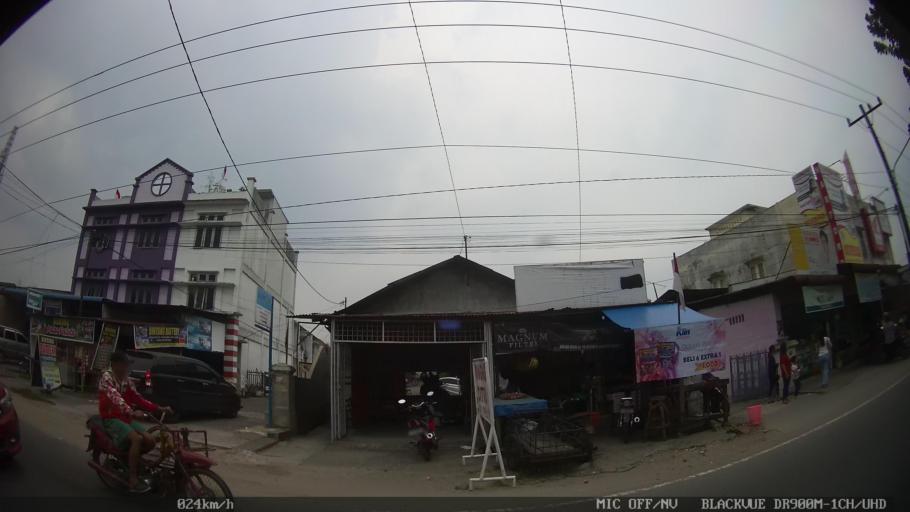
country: ID
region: North Sumatra
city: Medan
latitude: 3.5580
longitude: 98.7185
